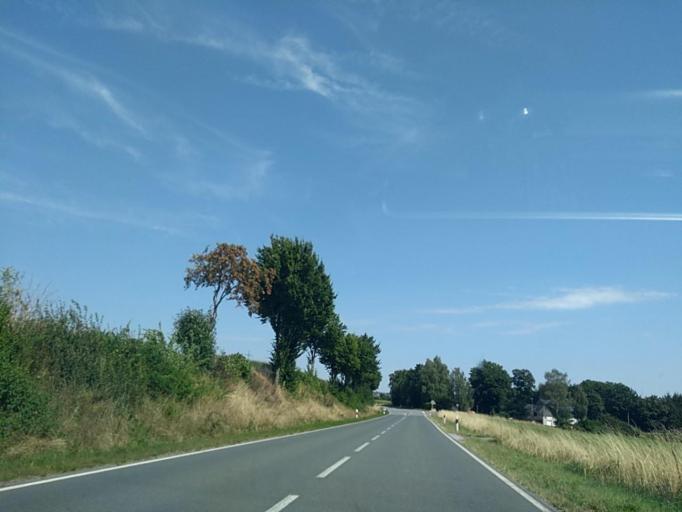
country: DE
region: North Rhine-Westphalia
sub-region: Regierungsbezirk Arnsberg
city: Brilon
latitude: 51.4226
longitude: 8.6177
